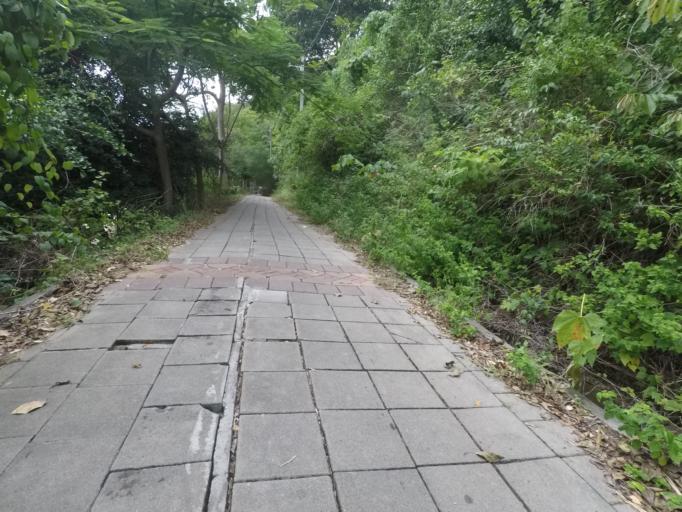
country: TH
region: Phangnga
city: Ban Phru Nai
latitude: 7.7713
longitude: 98.7673
